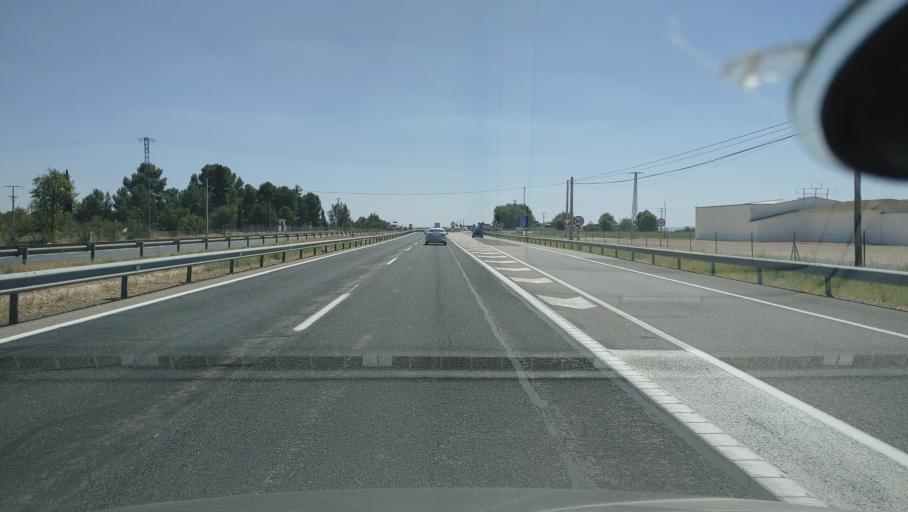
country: ES
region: Castille-La Mancha
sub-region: Provincia de Ciudad Real
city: Manzanares
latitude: 39.1140
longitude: -3.3775
